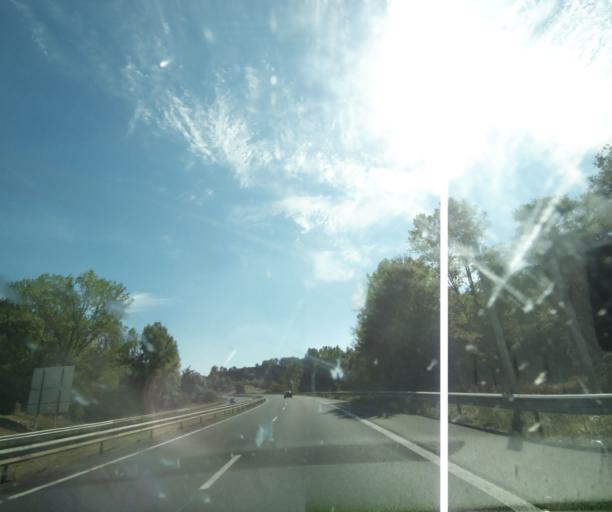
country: FR
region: Limousin
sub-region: Departement de la Correze
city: Brive-la-Gaillarde
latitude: 45.1311
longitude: 1.4917
